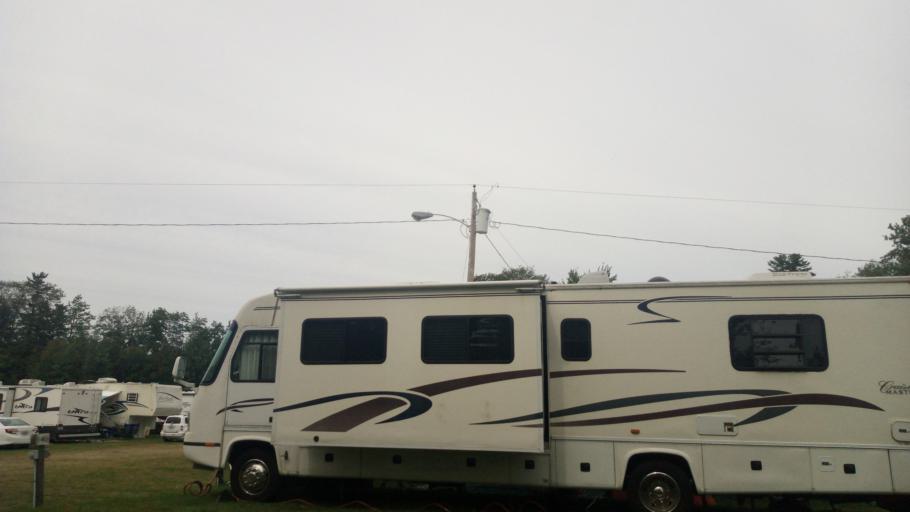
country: US
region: Maine
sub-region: Kennebec County
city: Windsor
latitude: 44.2881
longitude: -69.5932
